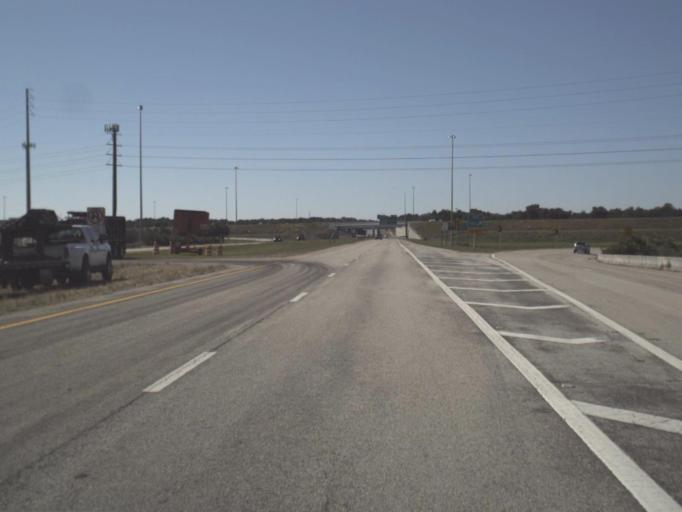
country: US
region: Florida
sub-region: Seminole County
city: Lake Mary
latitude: 28.7967
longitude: -81.3399
